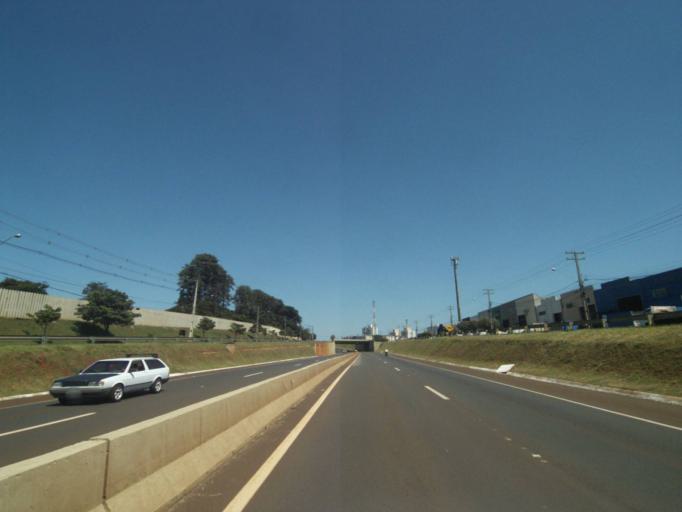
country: BR
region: Parana
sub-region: Londrina
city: Londrina
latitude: -23.3512
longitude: -51.1651
